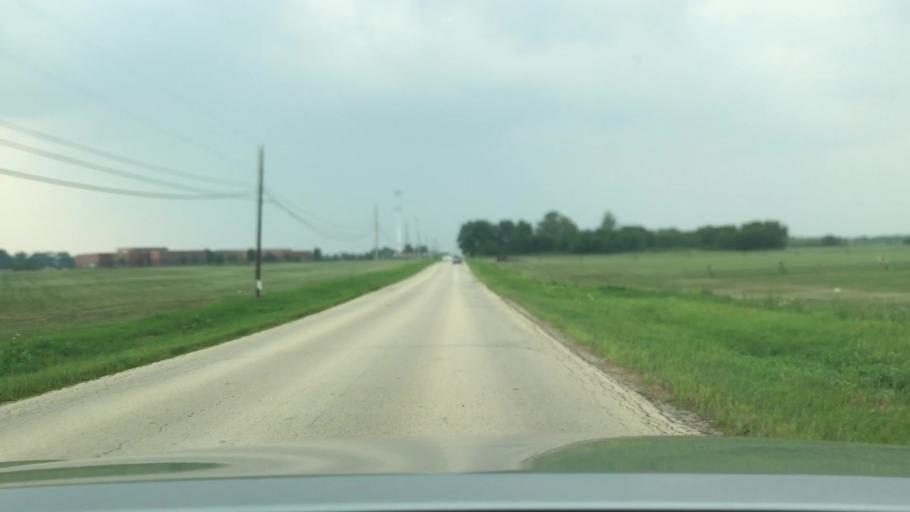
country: US
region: Illinois
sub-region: Will County
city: Plainfield
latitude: 41.6892
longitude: -88.2537
